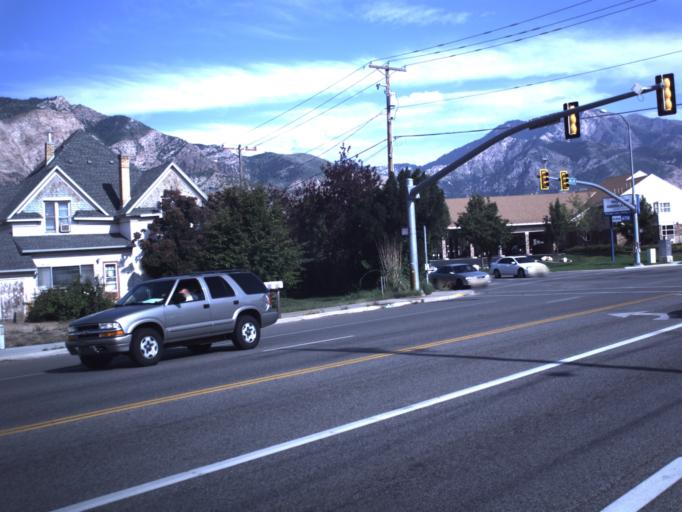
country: US
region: Utah
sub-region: Weber County
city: Harrisville
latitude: 41.2670
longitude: -111.9747
